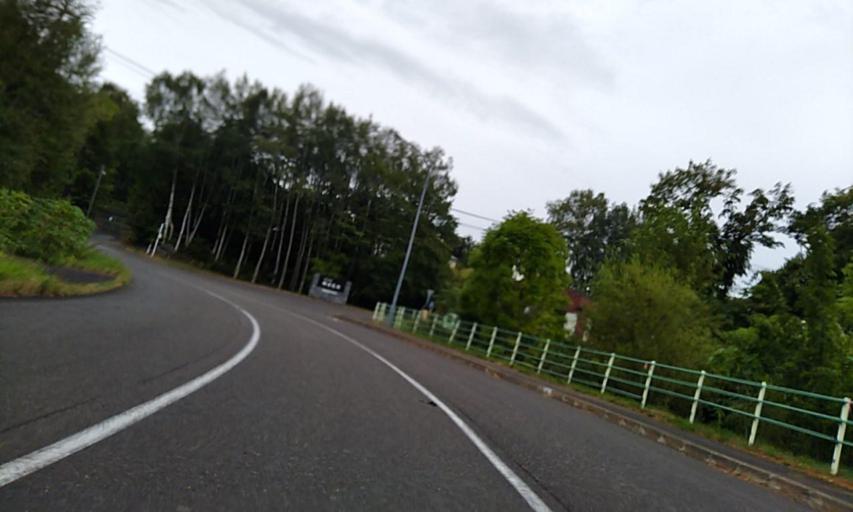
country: JP
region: Hokkaido
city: Abashiri
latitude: 43.9982
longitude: 144.2288
